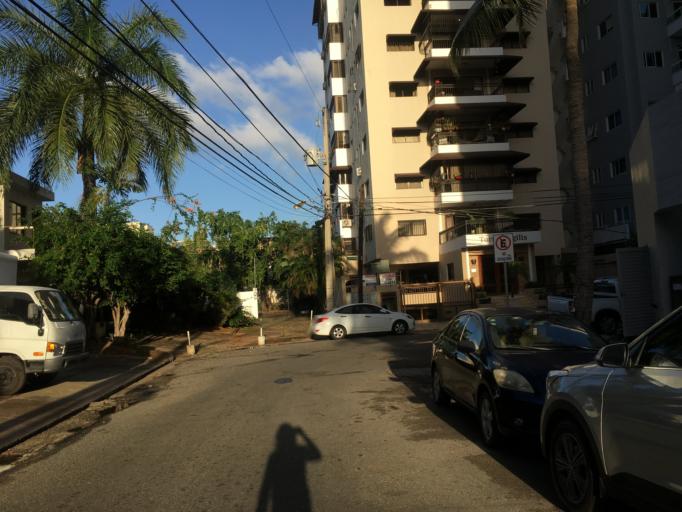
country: DO
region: Nacional
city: La Julia
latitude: 18.4625
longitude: -69.9319
